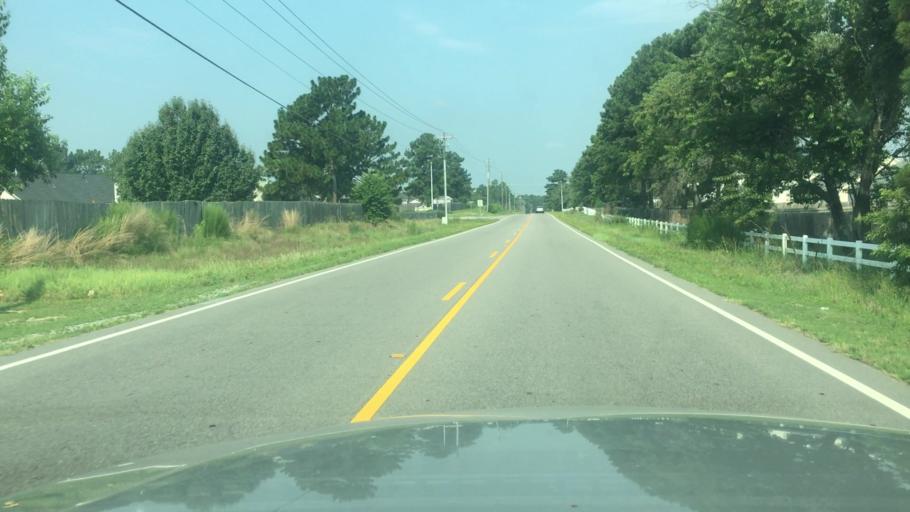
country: US
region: North Carolina
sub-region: Cumberland County
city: Hope Mills
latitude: 34.9999
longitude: -78.9439
